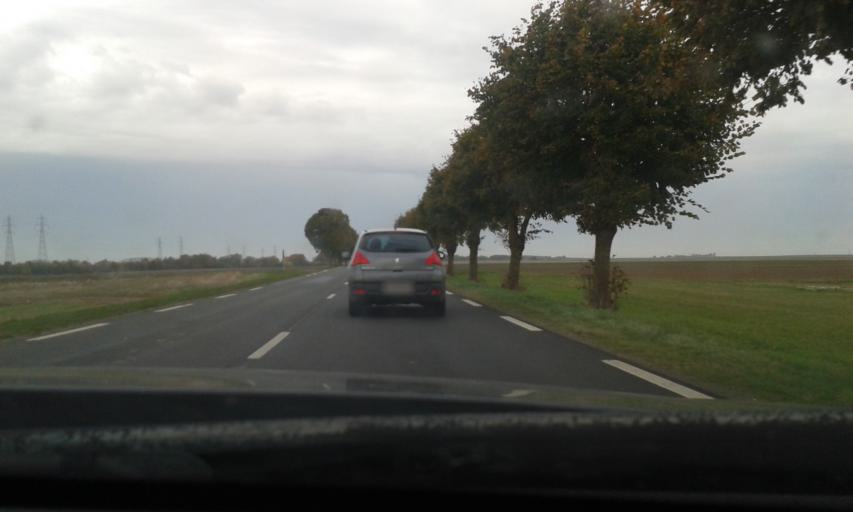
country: FR
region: Centre
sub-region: Departement d'Eure-et-Loir
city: Baigneaux
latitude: 48.1209
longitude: 1.8578
